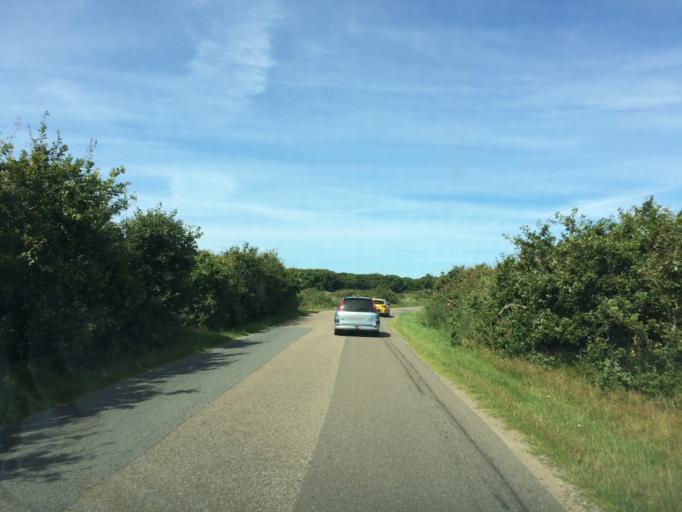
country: DK
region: South Denmark
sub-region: Varde Kommune
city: Oksbol
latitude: 55.6899
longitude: 8.1897
